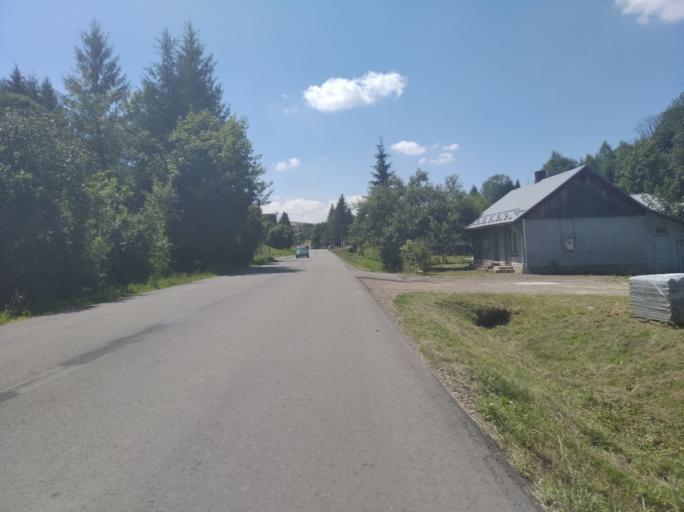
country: PL
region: Subcarpathian Voivodeship
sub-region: Powiat brzozowski
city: Jablonka
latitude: 49.6959
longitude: 22.1169
